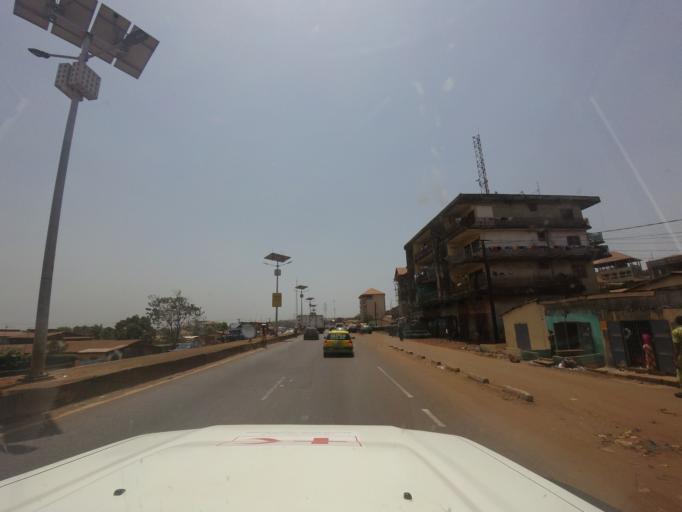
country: GN
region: Kindia
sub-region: Prefecture de Dubreka
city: Dubreka
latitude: 9.6480
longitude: -13.5584
